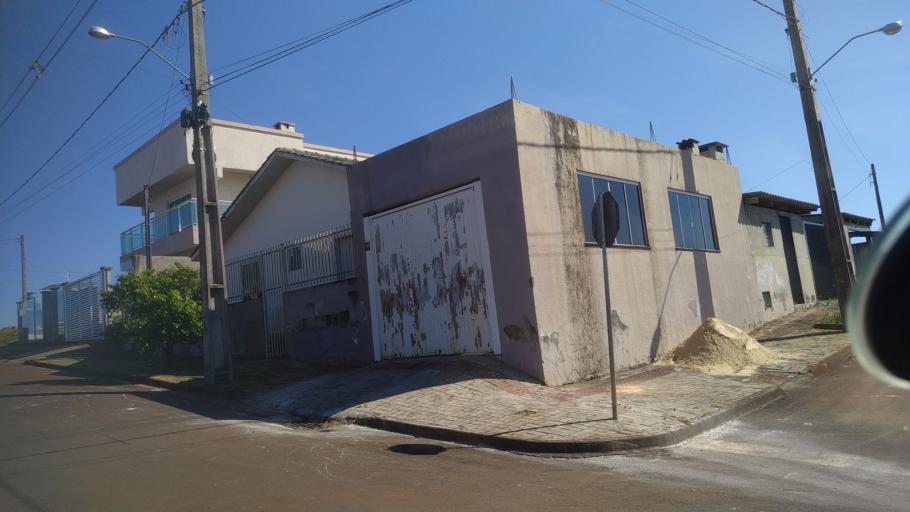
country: BR
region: Santa Catarina
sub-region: Chapeco
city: Chapeco
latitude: -27.0897
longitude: -52.5797
